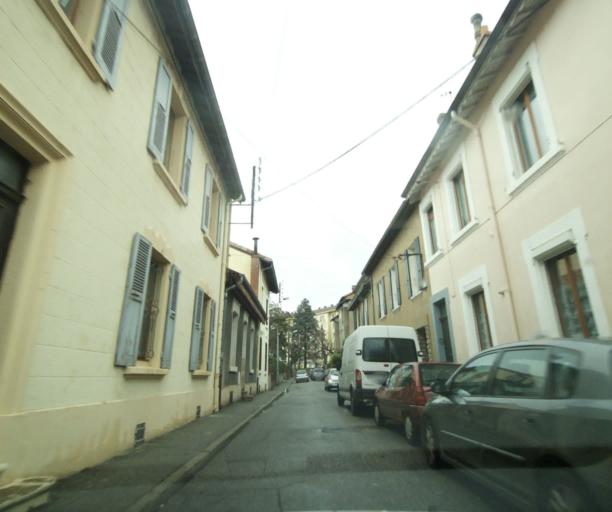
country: FR
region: Rhone-Alpes
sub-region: Departement de la Drome
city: Valence
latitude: 44.9374
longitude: 4.8939
